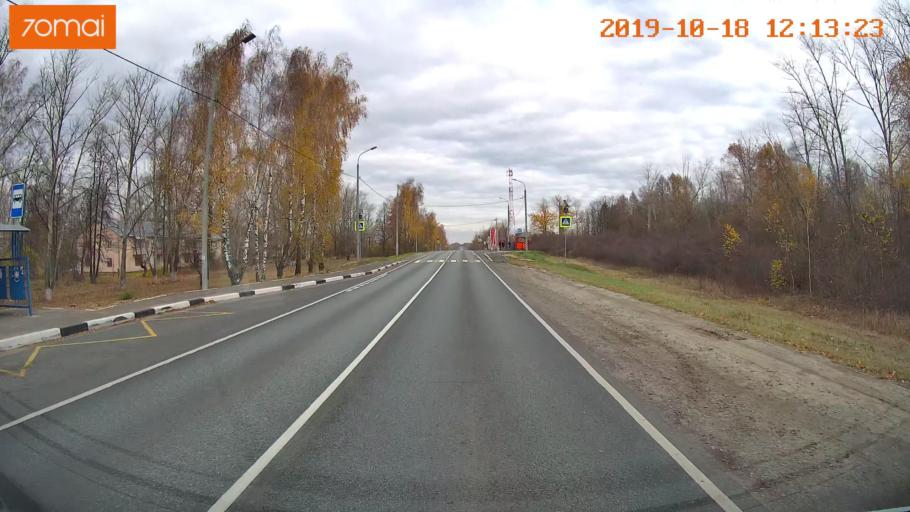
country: RU
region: Rjazan
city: Zakharovo
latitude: 54.4205
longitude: 39.3695
